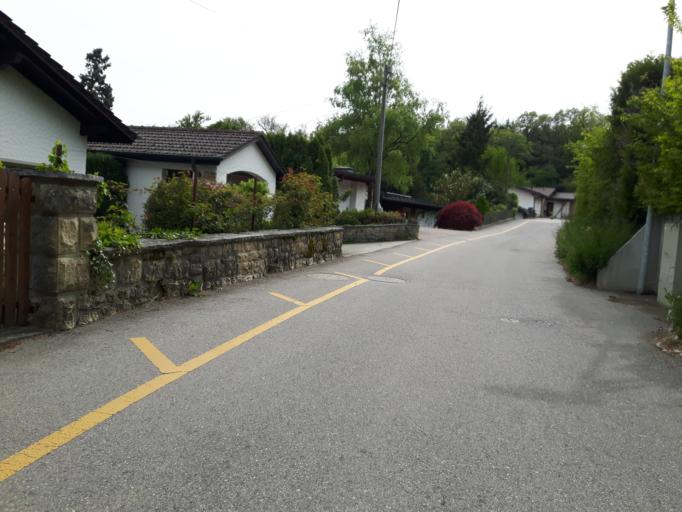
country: CH
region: Neuchatel
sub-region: Boudry District
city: Bevaix
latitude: 46.9255
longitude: 6.8066
